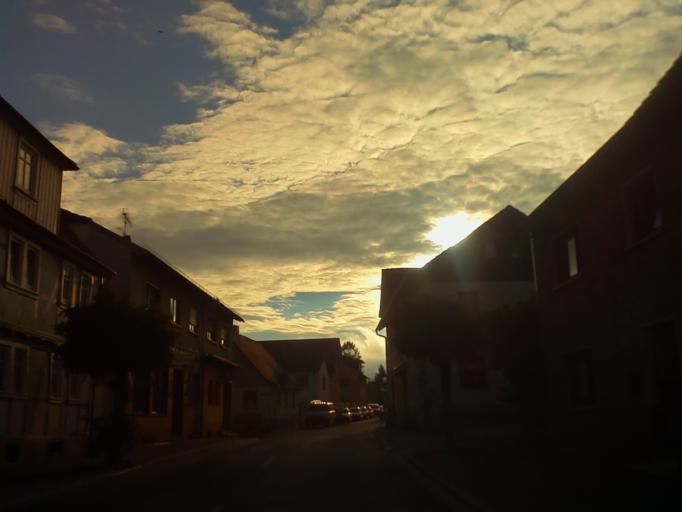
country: DE
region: Hesse
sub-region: Regierungsbezirk Darmstadt
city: Frankisch-Crumbach
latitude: 49.7453
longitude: 8.8548
